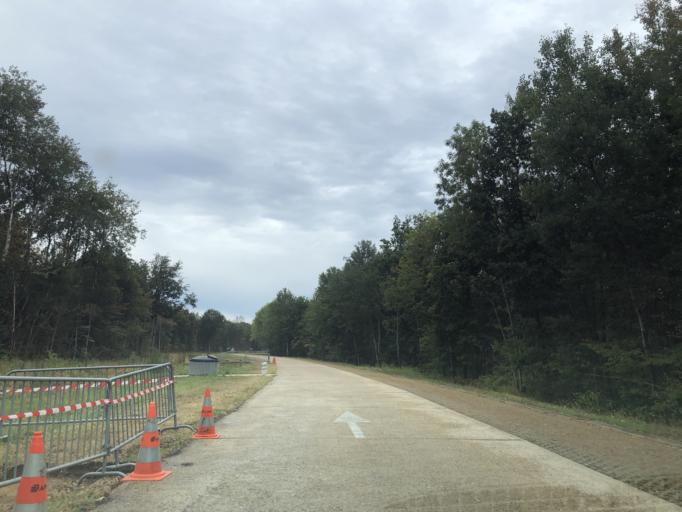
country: FR
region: Ile-de-France
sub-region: Departement de Seine-et-Marne
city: Montereau-Fault-Yonne
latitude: 48.4295
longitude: 2.9291
